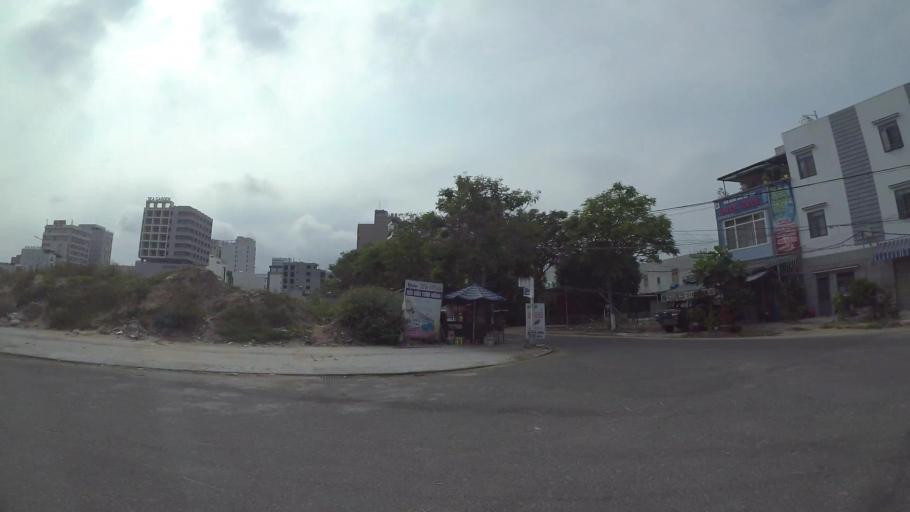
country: VN
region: Da Nang
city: Son Tra
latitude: 16.0714
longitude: 108.2396
